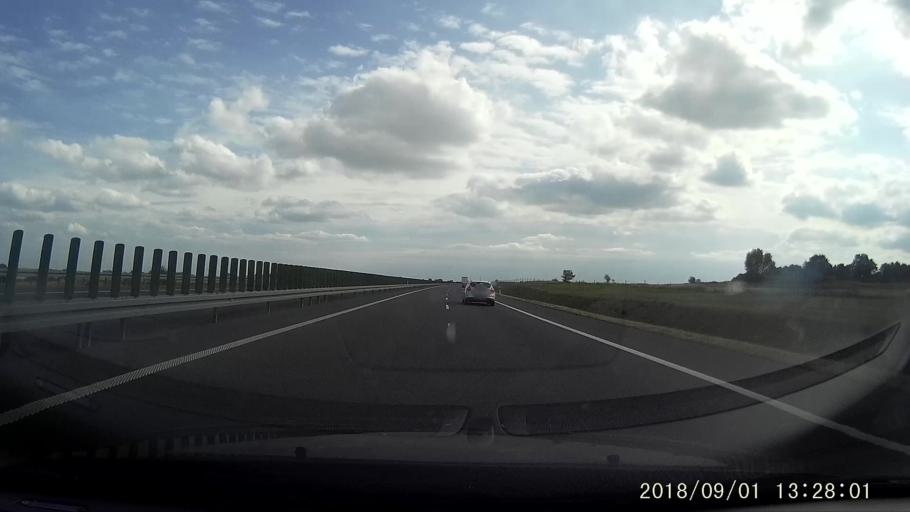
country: PL
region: West Pomeranian Voivodeship
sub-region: Powiat pyrzycki
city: Kozielice
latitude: 53.0809
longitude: 14.8496
